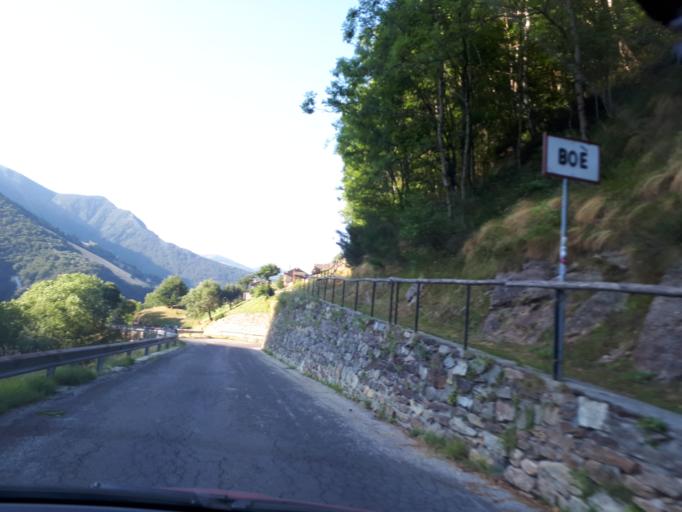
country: CH
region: Ticino
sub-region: Locarno District
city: Magadino
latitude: 46.1048
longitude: 8.8382
